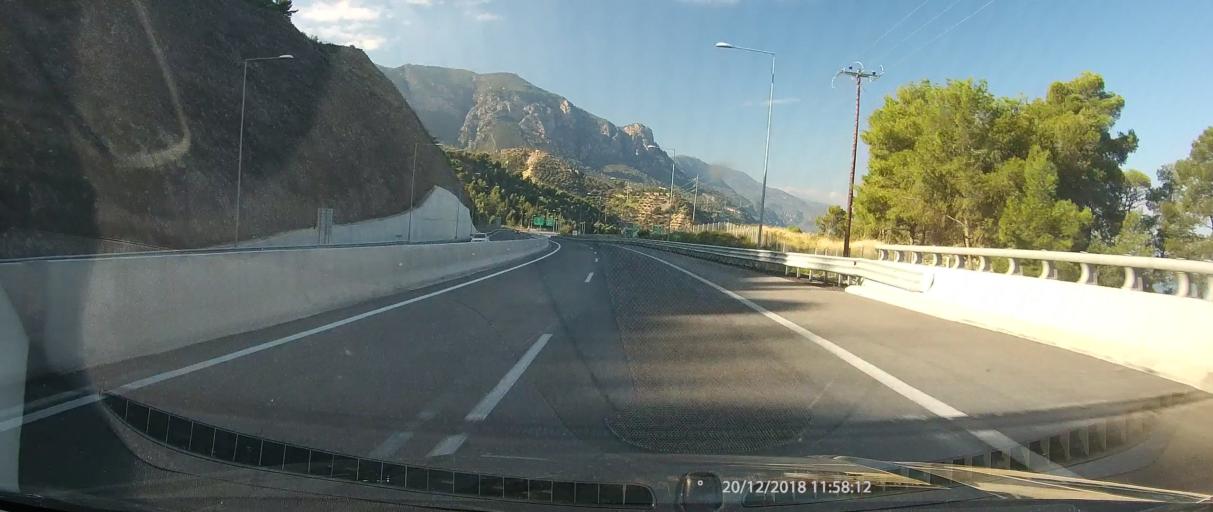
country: GR
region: West Greece
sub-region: Nomos Achaias
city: Akrata
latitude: 38.1749
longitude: 22.2520
